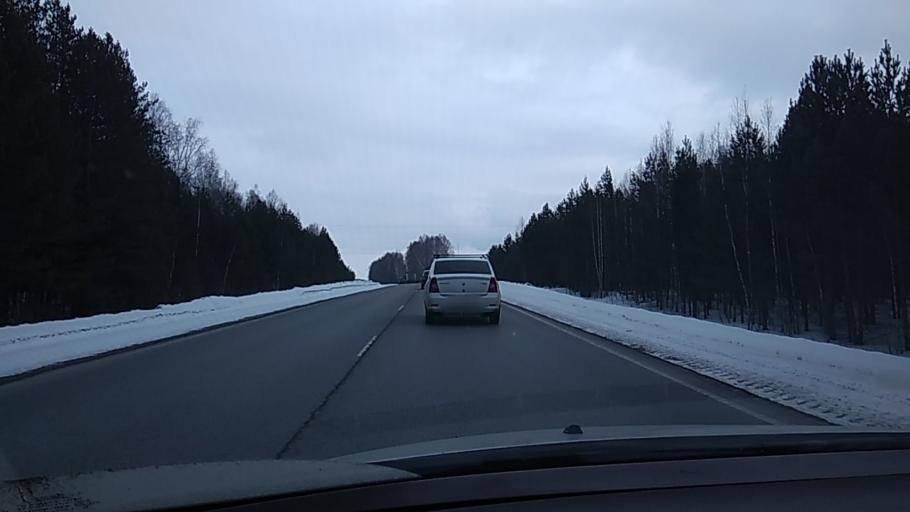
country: RU
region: Sverdlovsk
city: Sovkhoznyy
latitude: 56.5315
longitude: 61.4135
